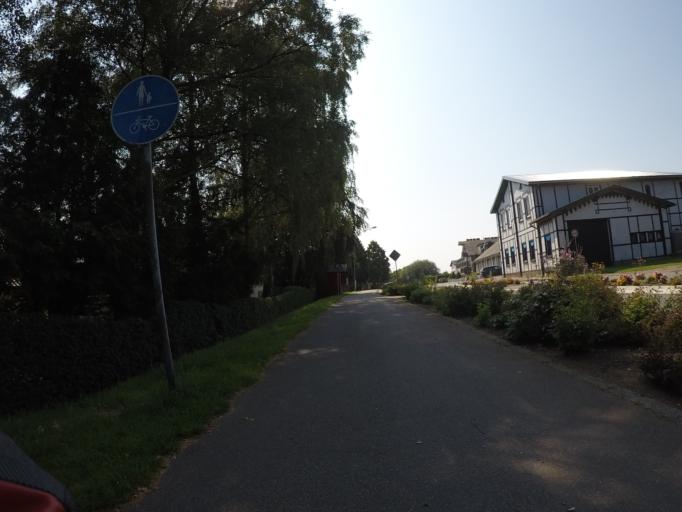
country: DE
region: Schleswig-Holstein
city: Sievershutten
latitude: 53.8445
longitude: 10.1114
